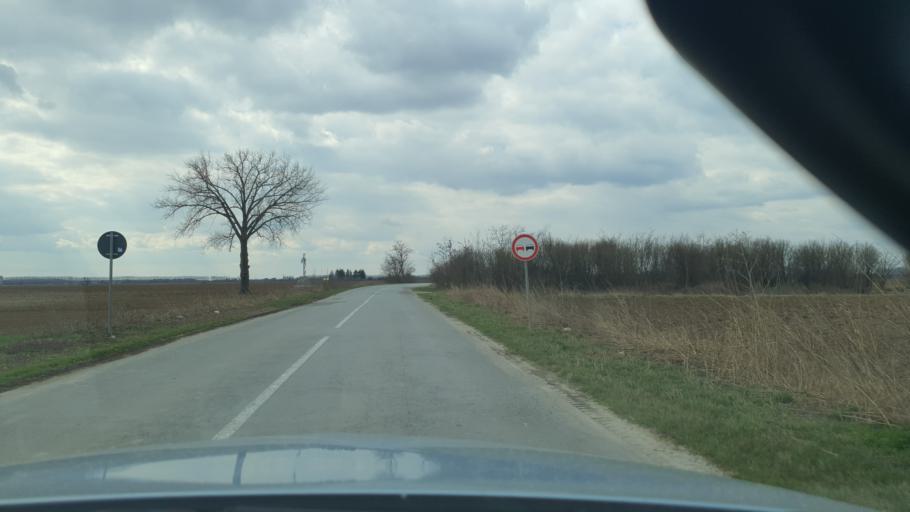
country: RS
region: Autonomna Pokrajina Vojvodina
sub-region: Juznobacki Okrug
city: Bac
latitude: 45.4004
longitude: 19.2785
